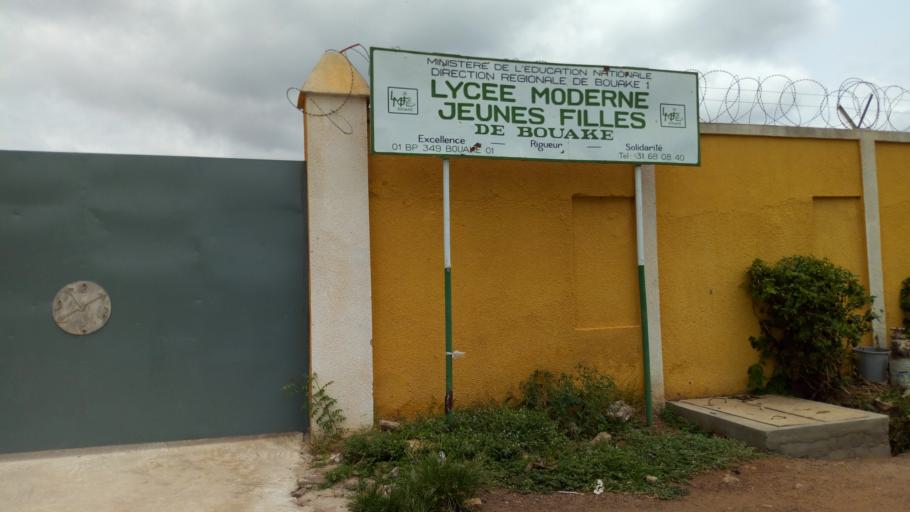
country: CI
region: Vallee du Bandama
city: Bouake
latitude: 7.6902
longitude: -5.0088
